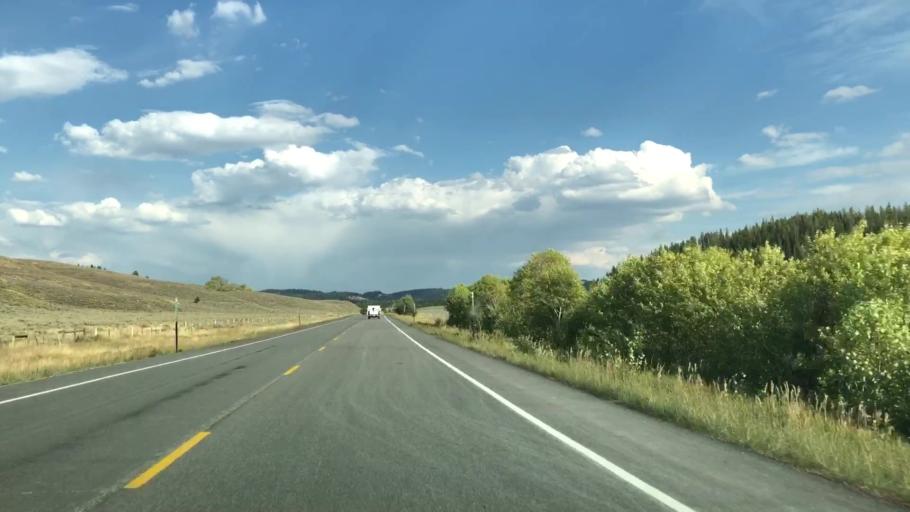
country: US
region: Wyoming
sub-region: Sublette County
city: Pinedale
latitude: 43.1521
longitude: -110.2819
